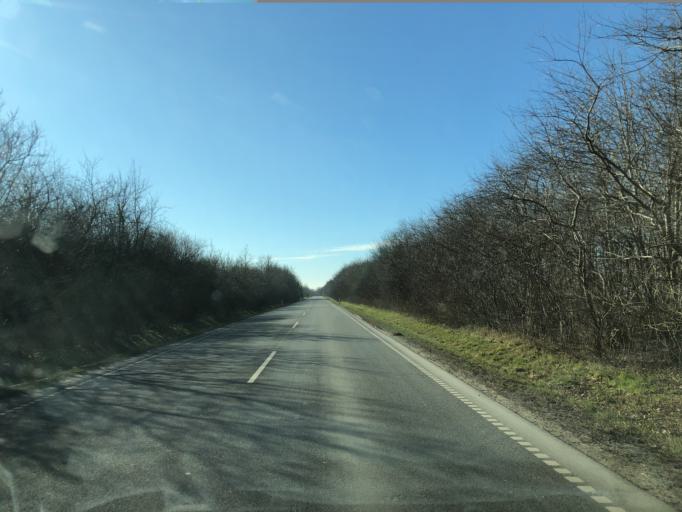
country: DK
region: Central Jutland
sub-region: Ikast-Brande Kommune
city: Bording Kirkeby
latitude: 56.1485
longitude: 9.2232
